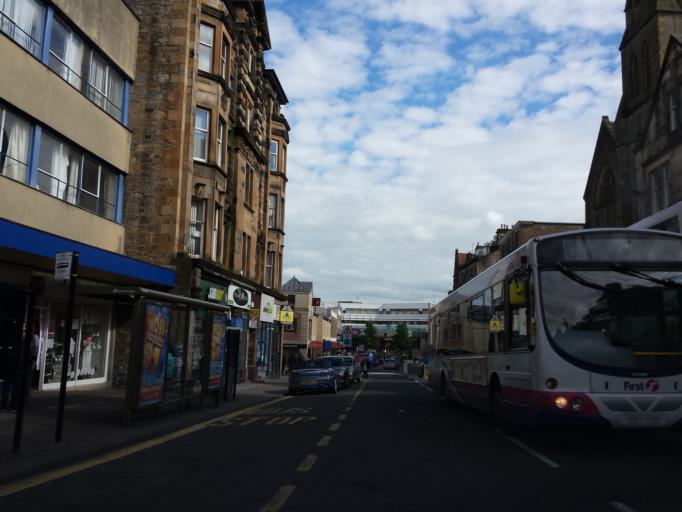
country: GB
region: Scotland
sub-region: Stirling
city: Stirling
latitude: 56.1195
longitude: -3.9374
